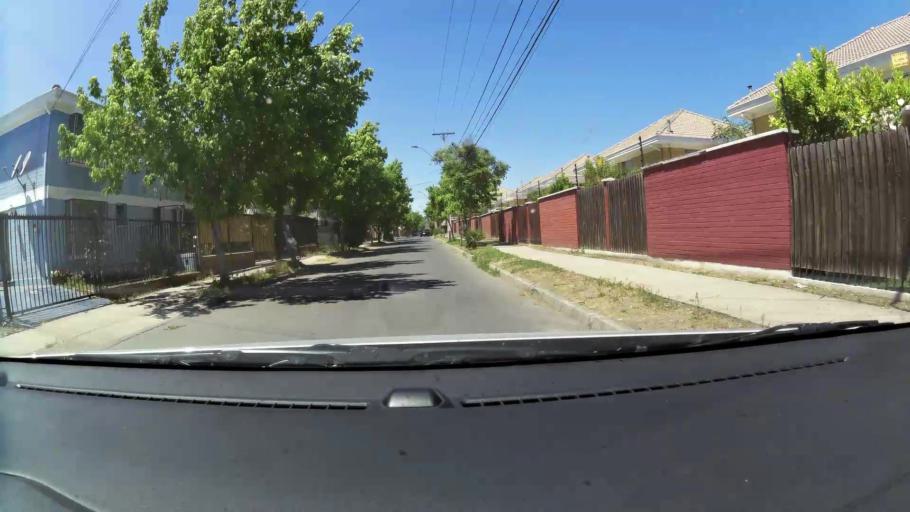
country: CL
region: Santiago Metropolitan
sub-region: Provincia de Maipo
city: San Bernardo
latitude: -33.6220
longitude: -70.7133
